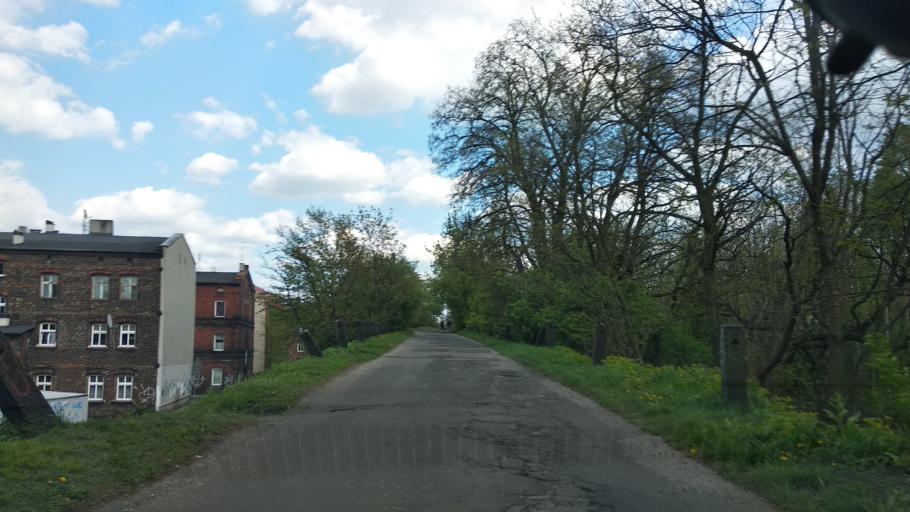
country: PL
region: Silesian Voivodeship
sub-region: Katowice
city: Katowice
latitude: 50.2626
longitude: 18.9960
